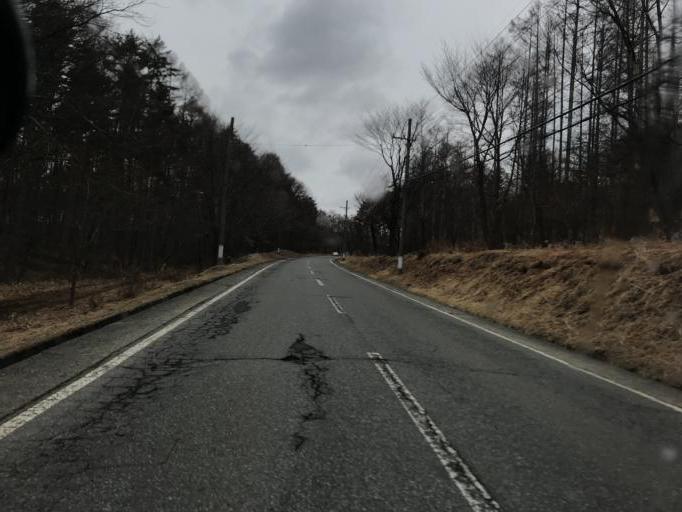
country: JP
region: Nagano
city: Chino
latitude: 35.9058
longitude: 138.3135
